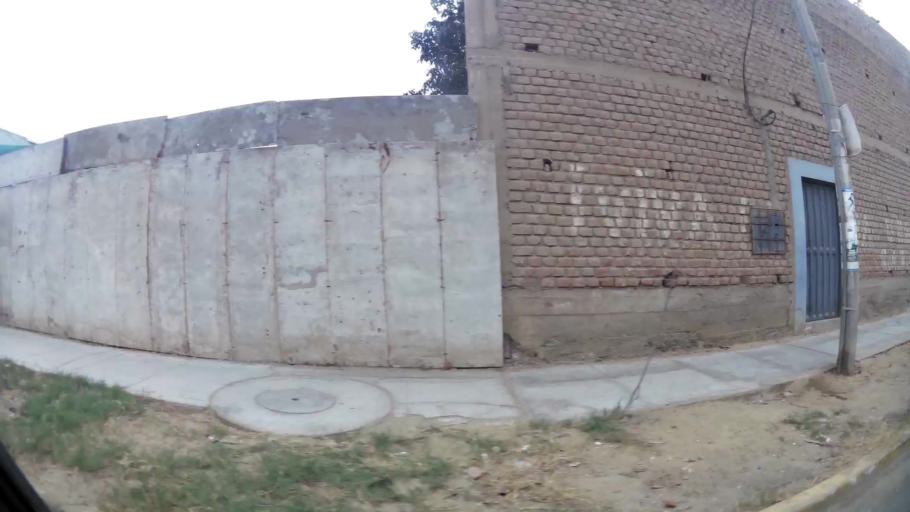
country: PE
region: La Libertad
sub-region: Provincia de Trujillo
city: Trujillo
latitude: -8.1101
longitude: -79.0397
